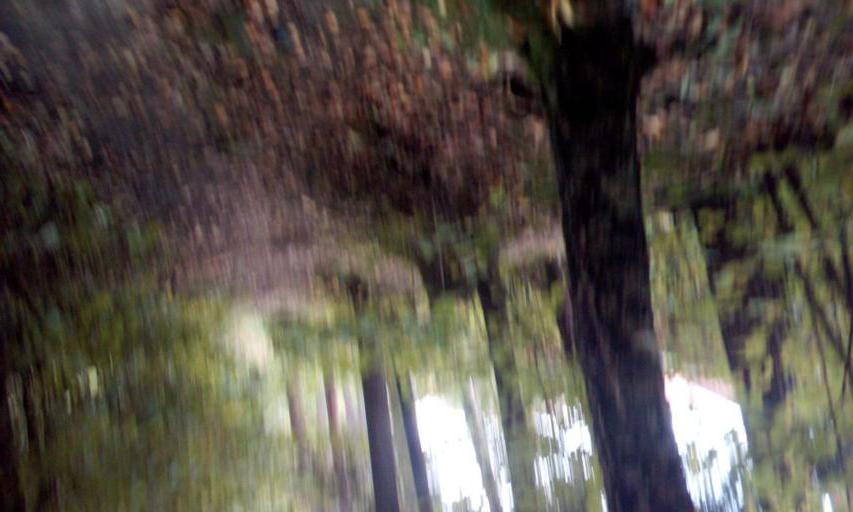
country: RU
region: Moskovskaya
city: Zhavoronki
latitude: 55.6648
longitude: 37.1172
